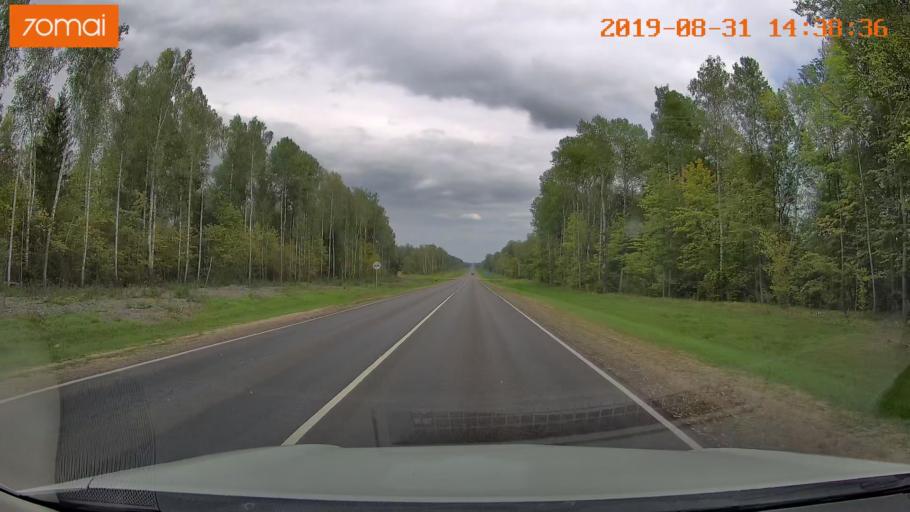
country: RU
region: Smolensk
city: Yekimovichi
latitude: 54.1856
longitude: 33.5323
